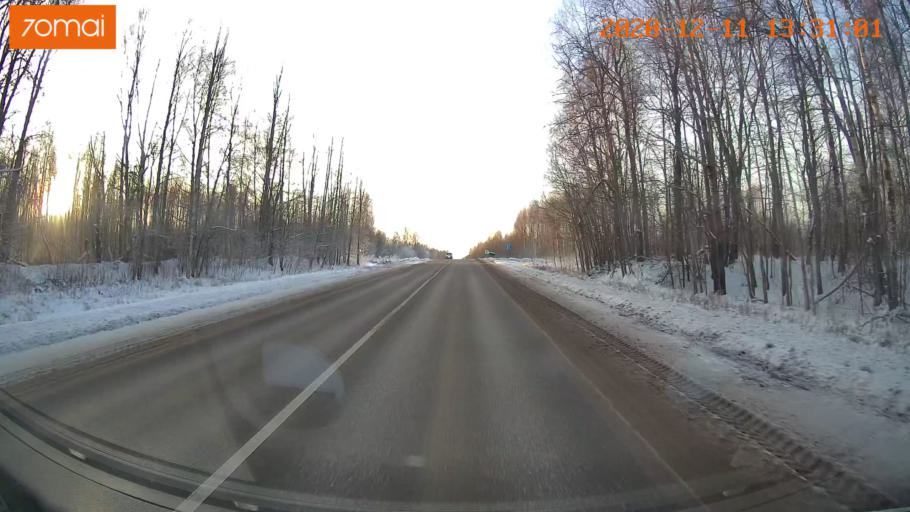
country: RU
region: Kostroma
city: Susanino
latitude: 57.9739
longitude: 41.3120
